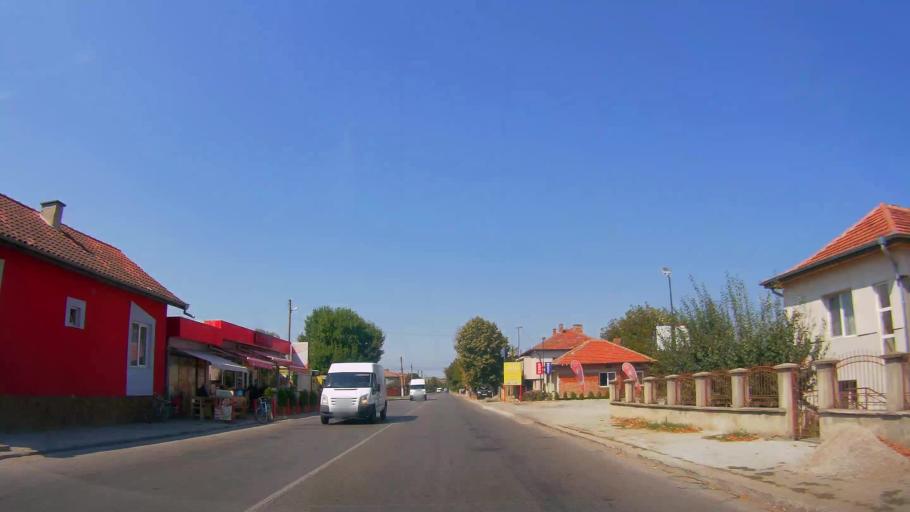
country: BG
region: Razgrad
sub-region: Obshtina Tsar Kaloyan
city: Tsar Kaloyan
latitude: 43.6033
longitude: 26.2434
